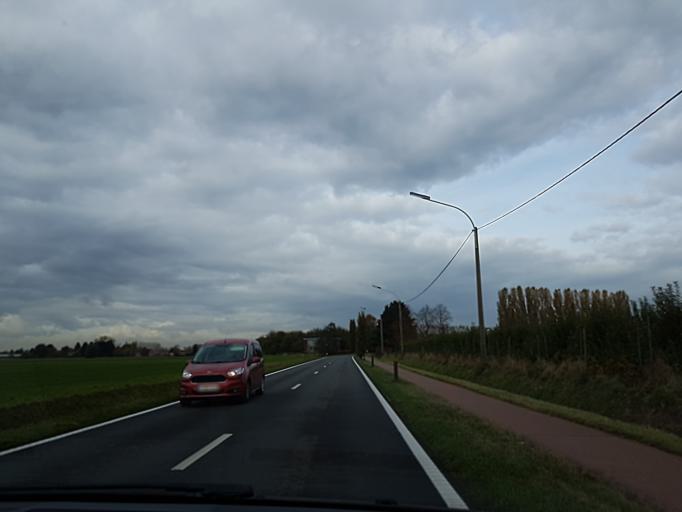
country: BE
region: Flanders
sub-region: Provincie Antwerpen
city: Ranst
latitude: 51.1750
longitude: 4.5625
